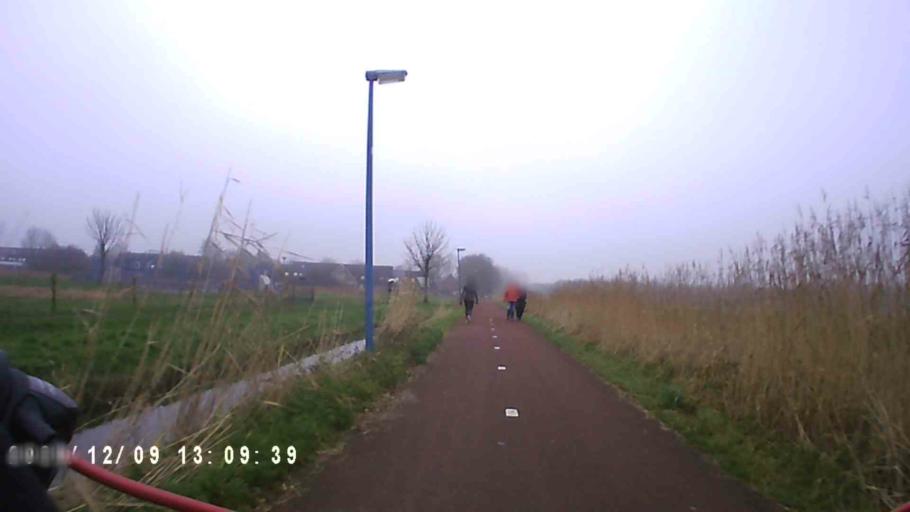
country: NL
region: Groningen
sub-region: Gemeente Groningen
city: Oosterpark
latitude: 53.2455
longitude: 6.6097
